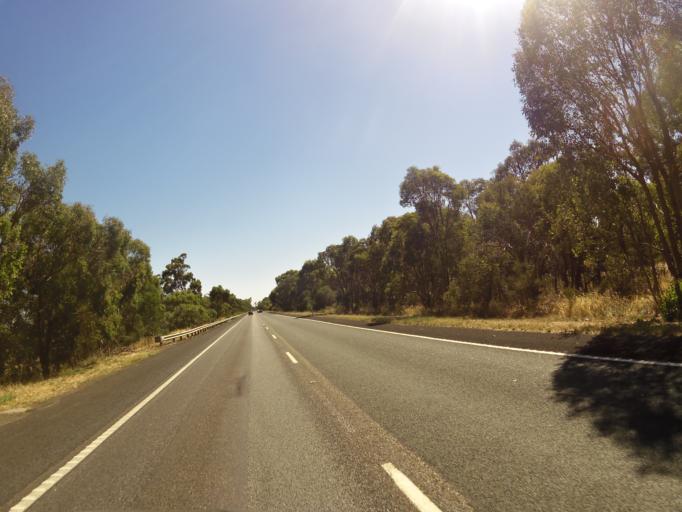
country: AU
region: Victoria
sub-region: Greater Shepparton
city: Shepparton
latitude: -36.8869
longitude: 145.2640
